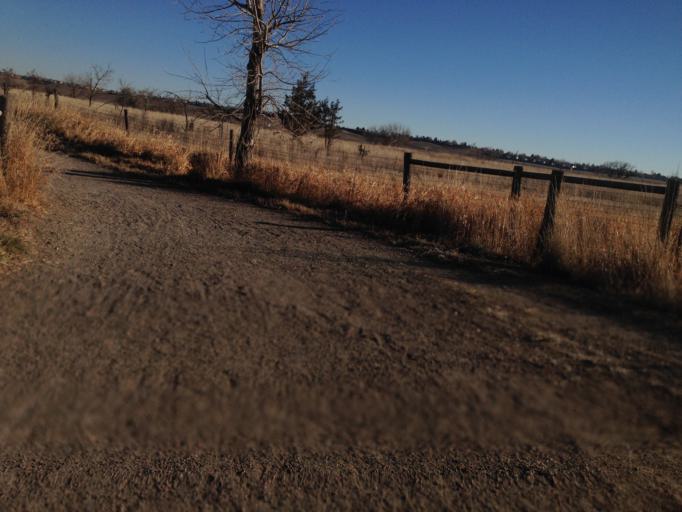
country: US
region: Colorado
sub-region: Broomfield County
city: Broomfield
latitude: 39.9466
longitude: -105.1090
